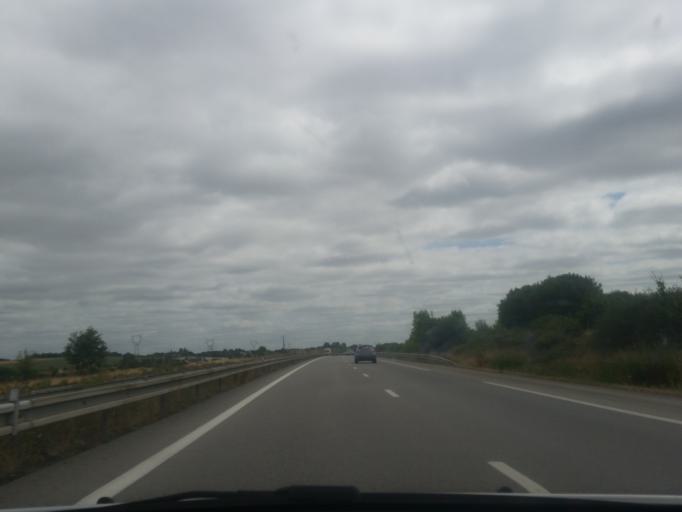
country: FR
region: Pays de la Loire
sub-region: Departement de la Loire-Atlantique
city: Saint-Herblon
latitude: 47.4199
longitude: -1.1109
